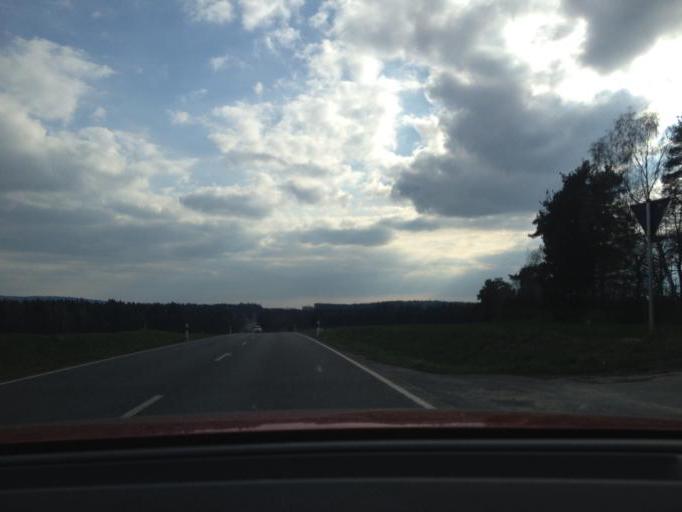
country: DE
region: Bavaria
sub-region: Upper Palatinate
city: Waldershof
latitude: 49.9707
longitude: 12.0436
